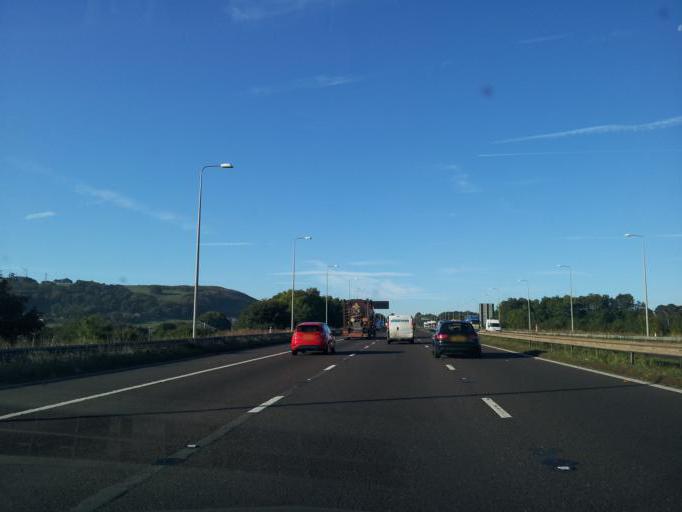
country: GB
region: England
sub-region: Kirklees
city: Linthwaite
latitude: 53.6560
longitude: -1.8723
